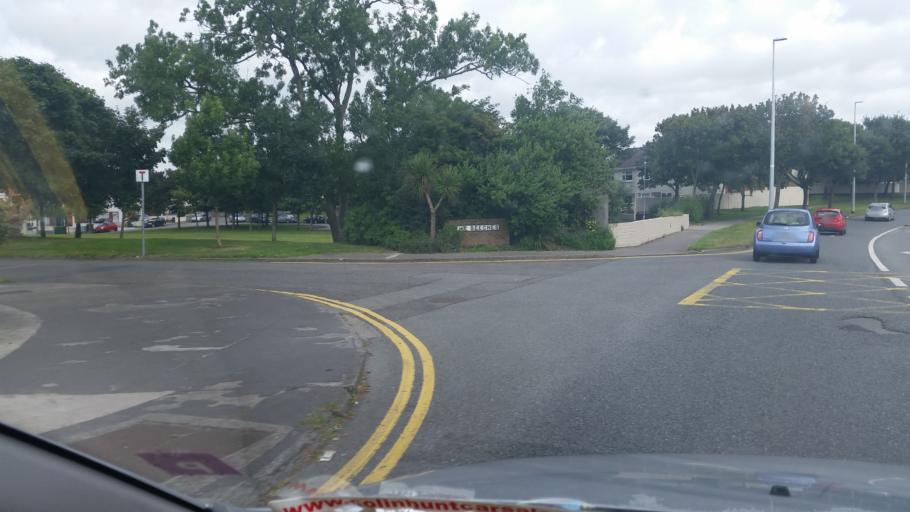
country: IE
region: Leinster
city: Donaghmede
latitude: 53.3924
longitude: -6.1674
